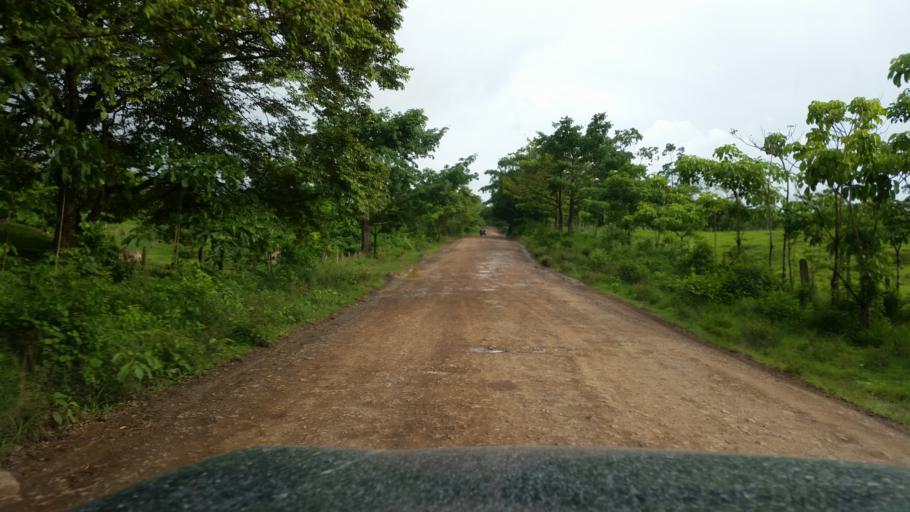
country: NI
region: Atlantico Norte (RAAN)
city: Siuna
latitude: 13.4197
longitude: -84.8532
